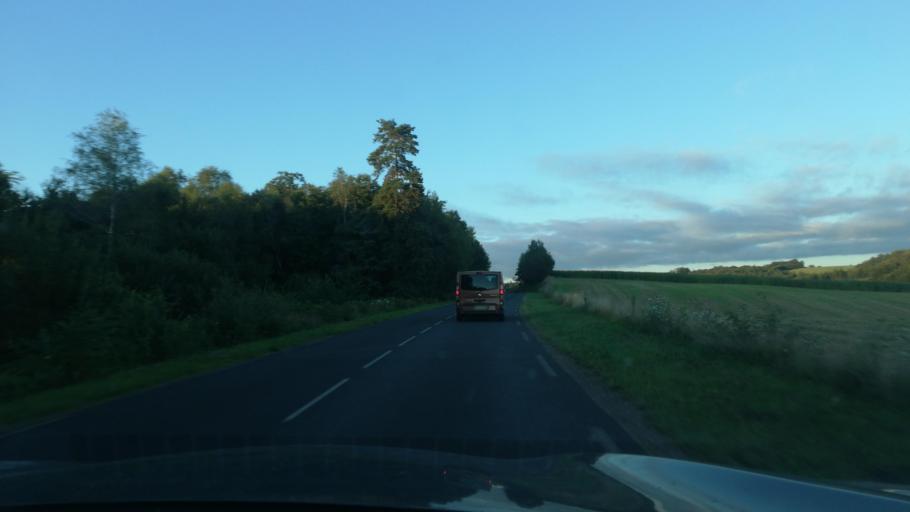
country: FR
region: Auvergne
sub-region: Departement du Cantal
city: Laroquebrou
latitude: 44.9434
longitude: 2.0873
